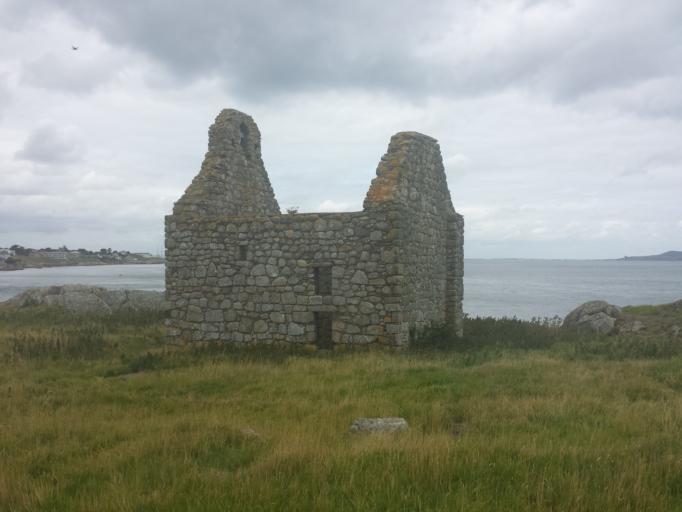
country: IE
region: Leinster
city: Dalkey
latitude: 53.2725
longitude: -6.0854
